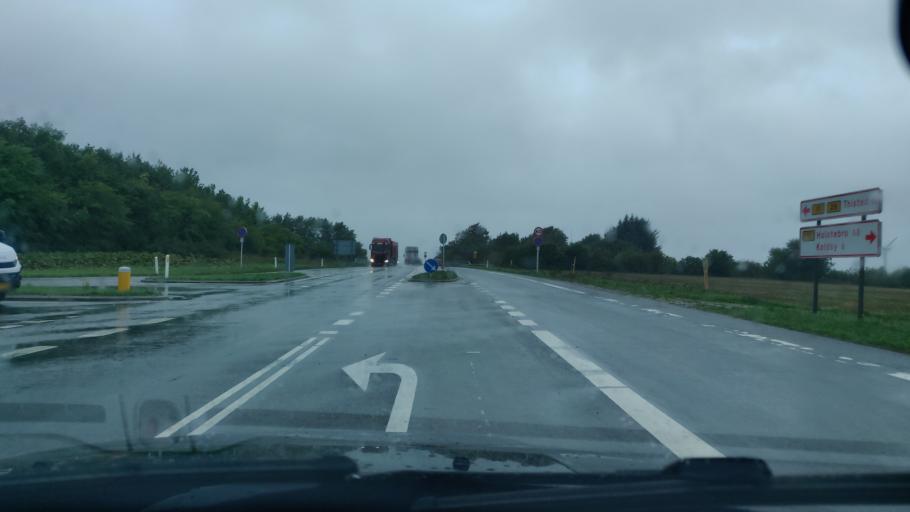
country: DK
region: North Denmark
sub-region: Thisted Kommune
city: Thisted
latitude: 56.8829
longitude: 8.5950
